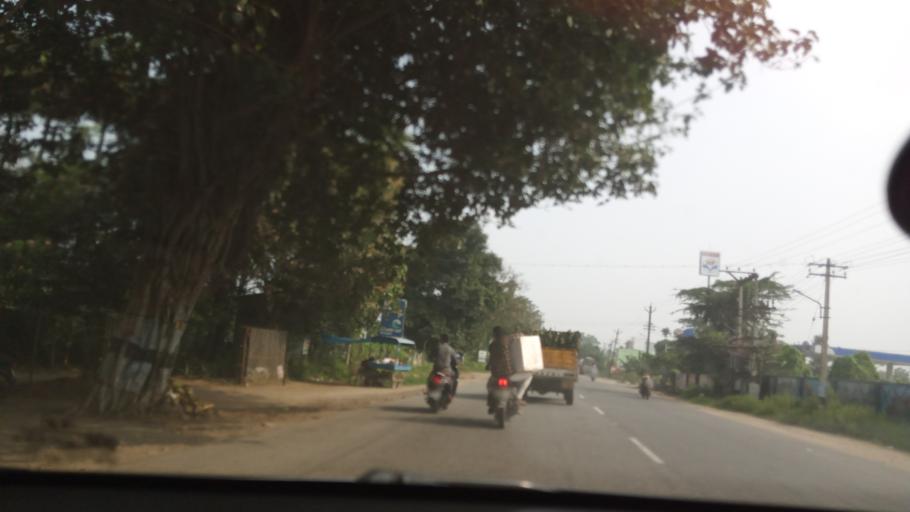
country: IN
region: Tamil Nadu
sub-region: Erode
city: Punjai Puliyampatti
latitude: 11.3429
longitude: 77.1610
